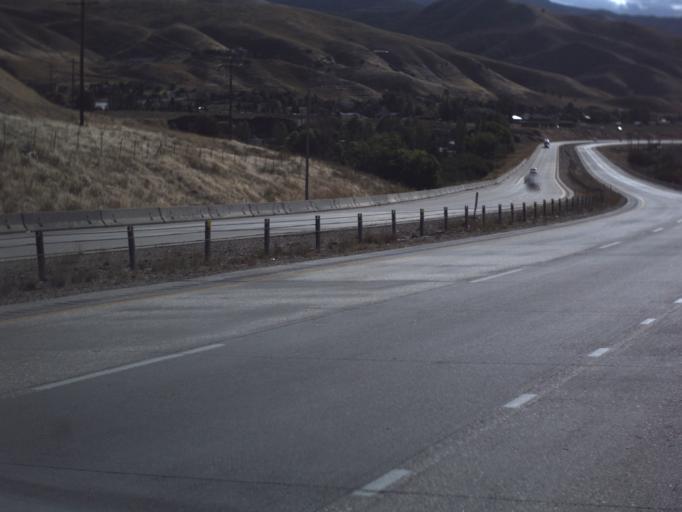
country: US
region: Utah
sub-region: Morgan County
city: Mountain Green
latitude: 41.1128
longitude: -111.7611
